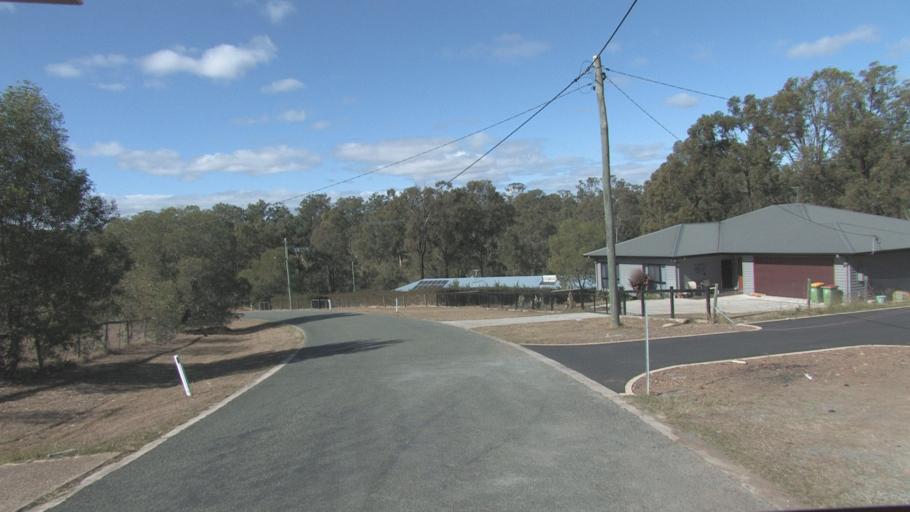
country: AU
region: Queensland
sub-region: Logan
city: Cedar Vale
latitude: -27.8823
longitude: 153.0057
